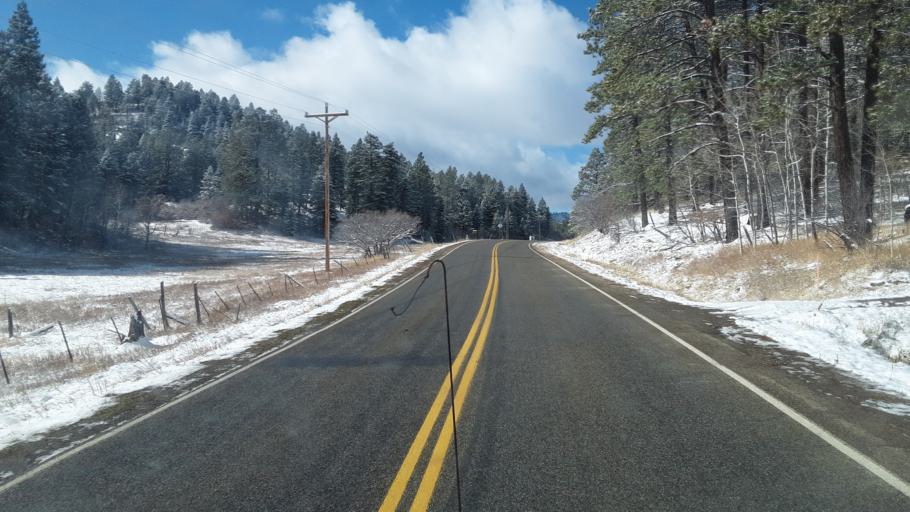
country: US
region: Colorado
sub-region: La Plata County
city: Bayfield
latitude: 37.3566
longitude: -107.6589
